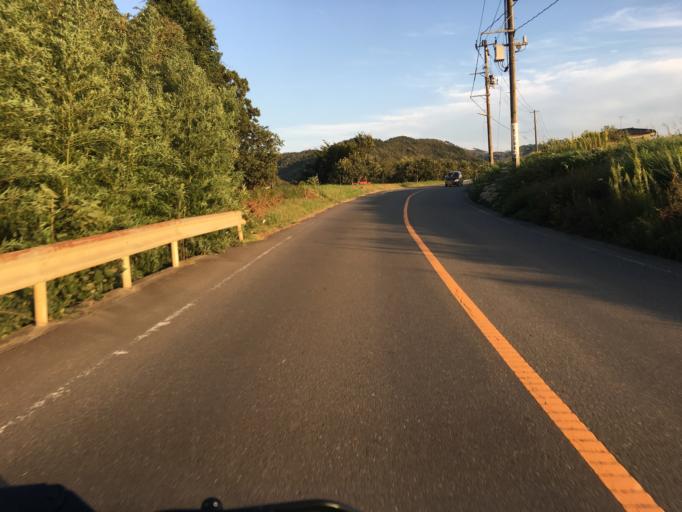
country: JP
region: Fukushima
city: Yanagawamachi-saiwaicho
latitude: 37.8476
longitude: 140.6134
